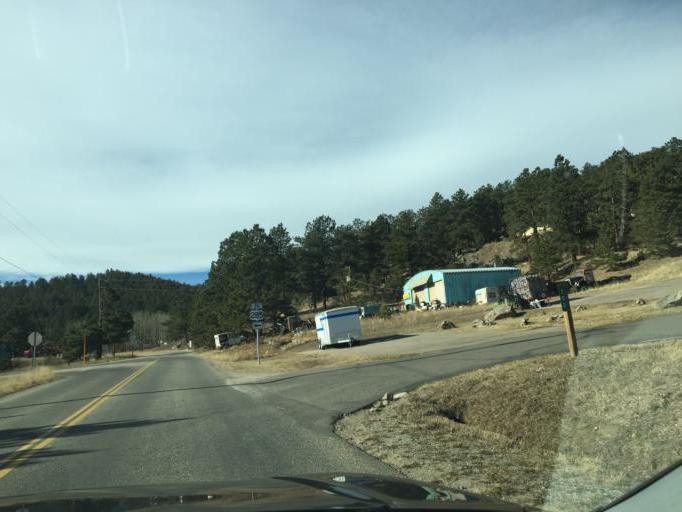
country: US
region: Colorado
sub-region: Jefferson County
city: Evergreen
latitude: 39.4365
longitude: -105.4612
